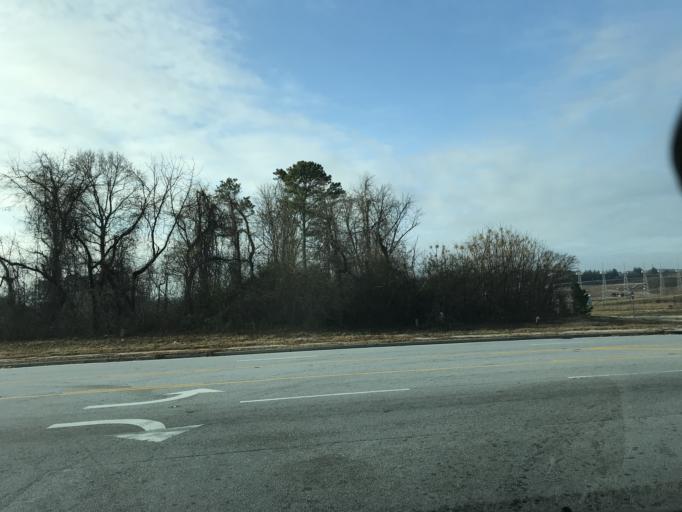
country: US
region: Georgia
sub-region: Fulton County
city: Hapeville
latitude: 33.6219
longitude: -84.4077
